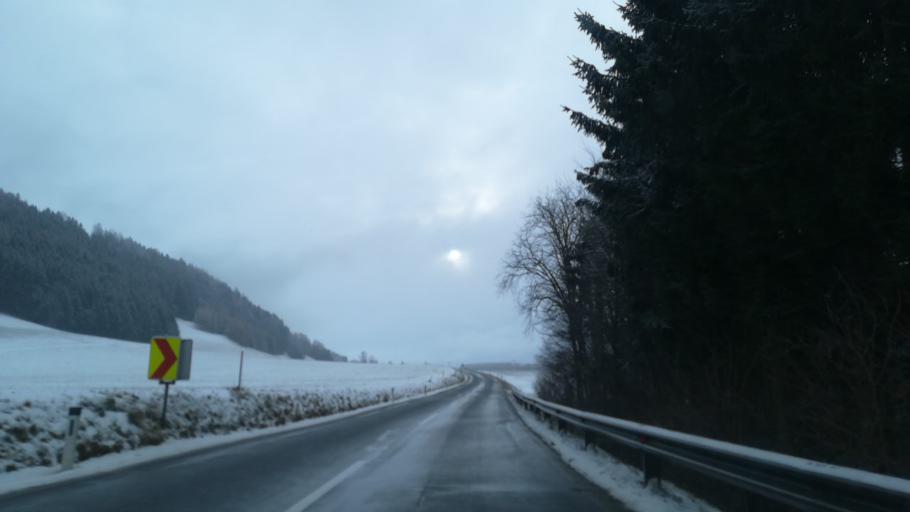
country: AT
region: Styria
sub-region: Politischer Bezirk Murtal
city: Poels
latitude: 47.2174
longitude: 14.6139
